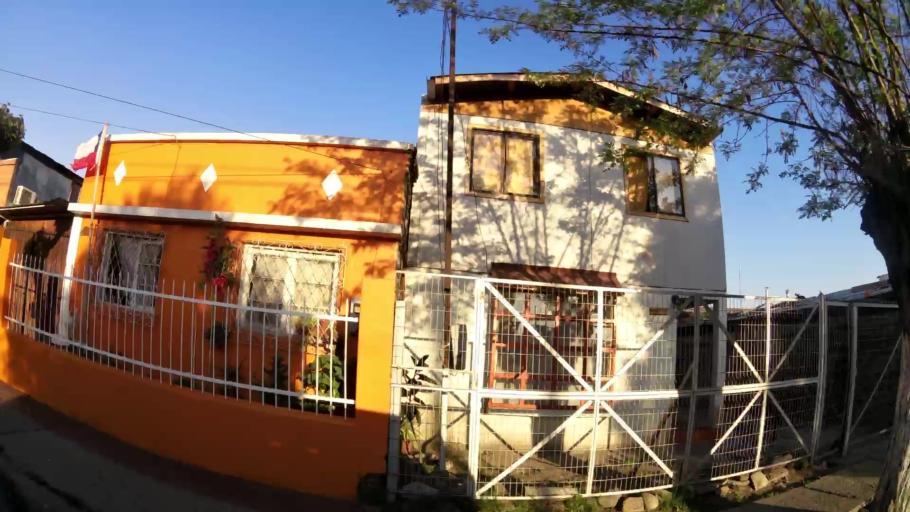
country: CL
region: Santiago Metropolitan
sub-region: Provincia de Santiago
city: La Pintana
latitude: -33.5224
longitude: -70.6224
